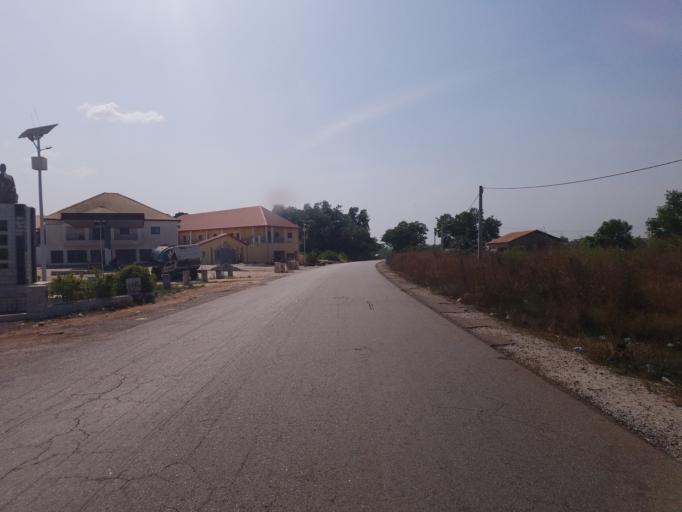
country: GN
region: Boke
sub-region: Fria
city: Fria
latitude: 10.0739
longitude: -13.7052
